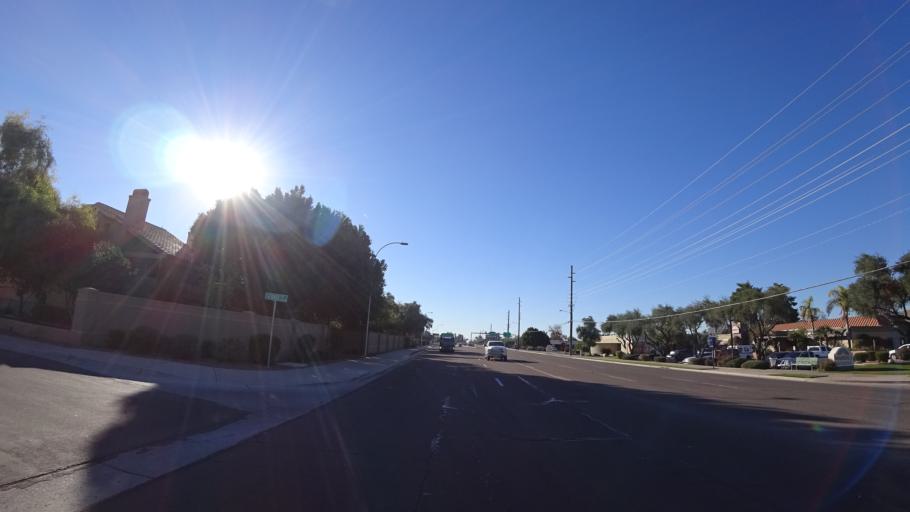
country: US
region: Arizona
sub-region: Maricopa County
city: Tempe
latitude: 33.3929
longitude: -111.8879
